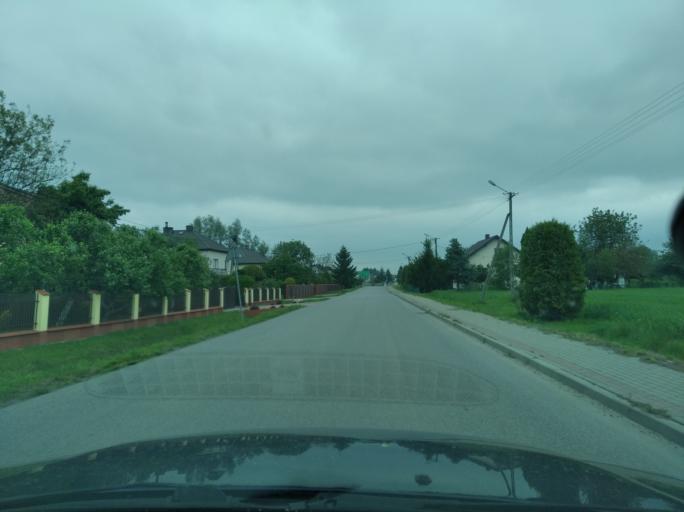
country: PL
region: Subcarpathian Voivodeship
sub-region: Powiat ropczycko-sedziszowski
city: Sedziszow Malopolski
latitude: 50.0946
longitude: 21.6641
